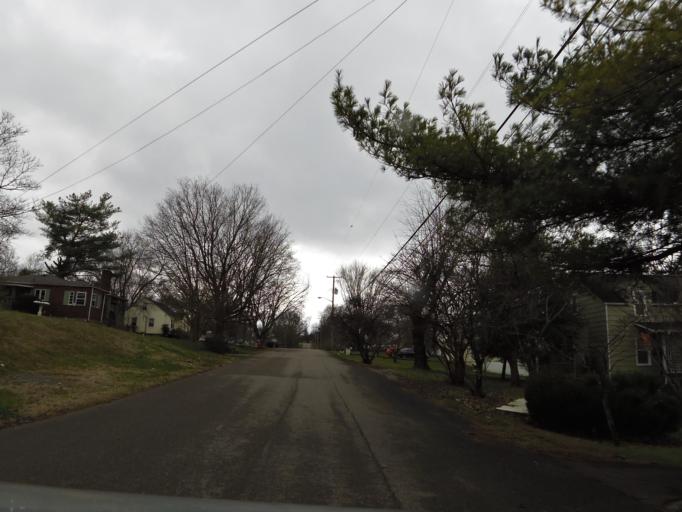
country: US
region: Tennessee
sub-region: Knox County
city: Knoxville
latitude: 36.0005
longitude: -83.9752
